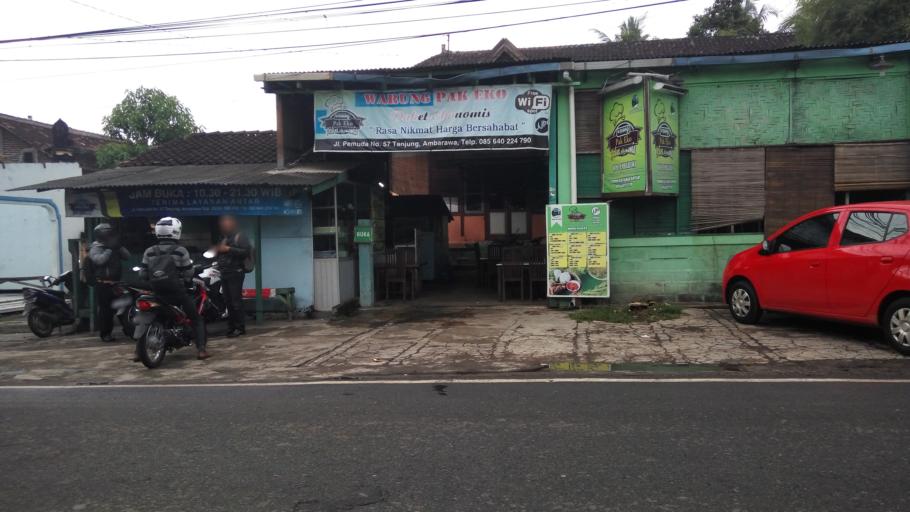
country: ID
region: Central Java
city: Ambarawa
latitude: -7.2660
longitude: 110.4045
